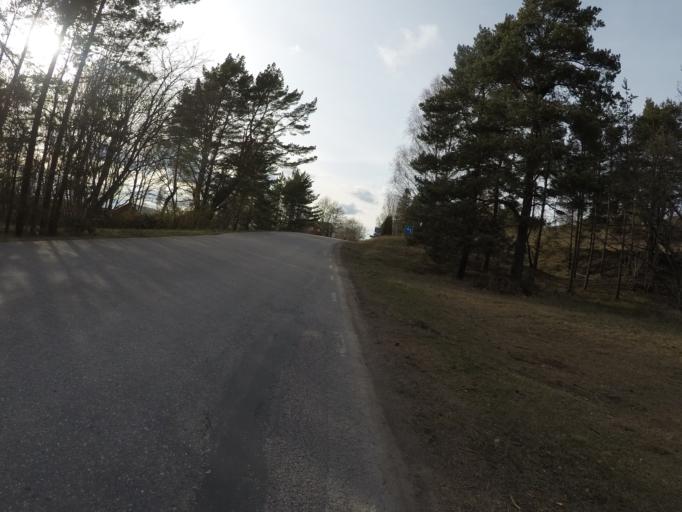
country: SE
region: Soedermanland
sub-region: Eskilstuna Kommun
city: Eskilstuna
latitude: 59.4341
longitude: 16.5560
